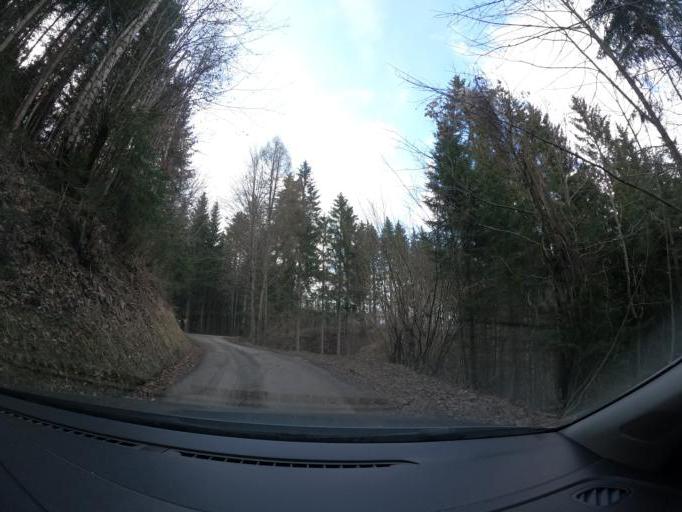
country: AT
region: Salzburg
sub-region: Politischer Bezirk Sankt Johann im Pongau
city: Pfarrwerfen
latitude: 47.4517
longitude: 13.1938
